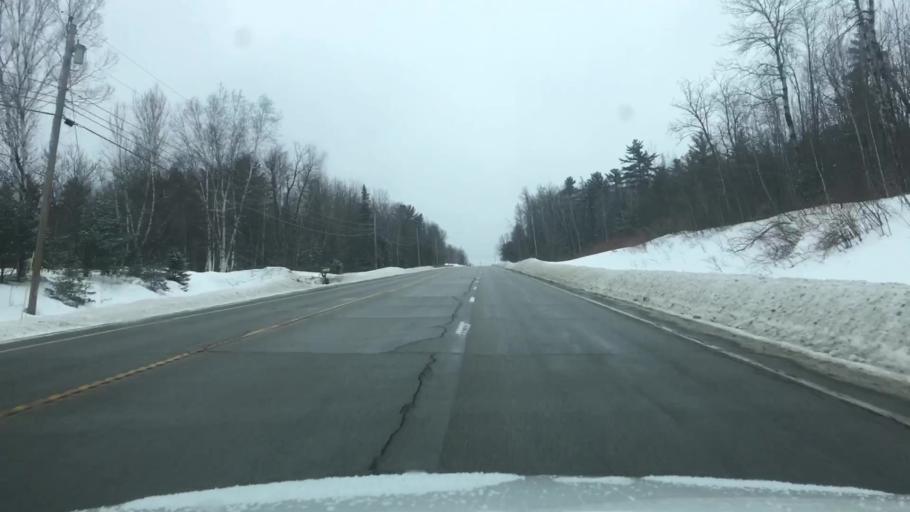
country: US
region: Maine
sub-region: Oxford County
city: Peru
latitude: 44.5770
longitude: -70.3702
